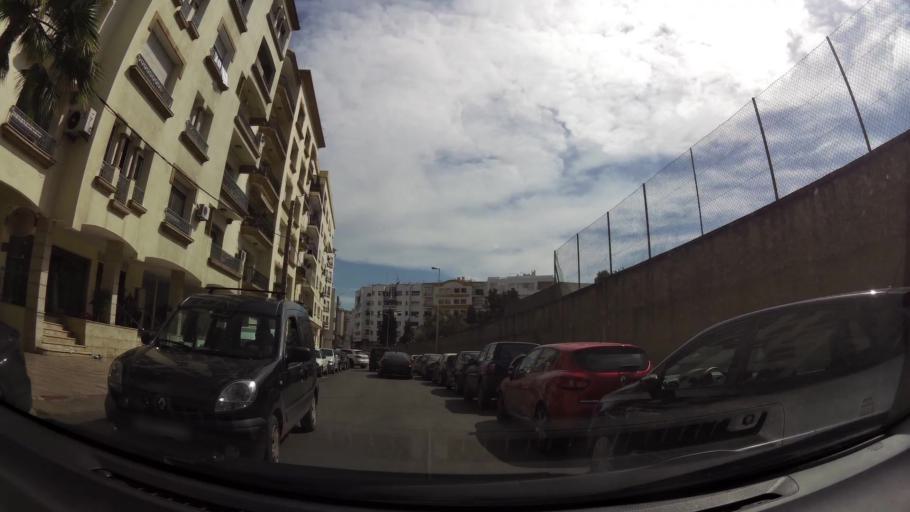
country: MA
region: Grand Casablanca
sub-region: Casablanca
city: Casablanca
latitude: 33.5863
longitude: -7.6425
